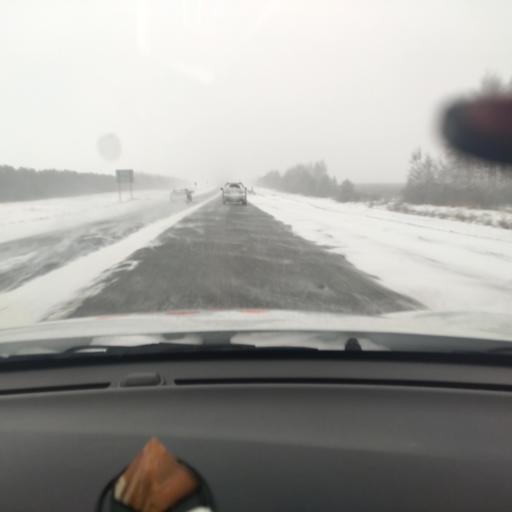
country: RU
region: Tatarstan
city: Verkhniy Uslon
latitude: 55.6648
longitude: 48.8618
